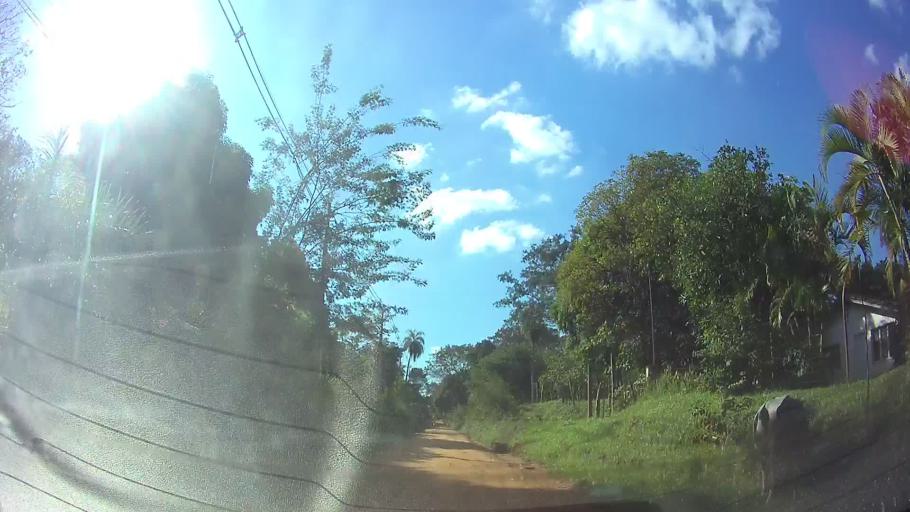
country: PY
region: Central
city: Limpio
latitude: -25.2524
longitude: -57.4748
